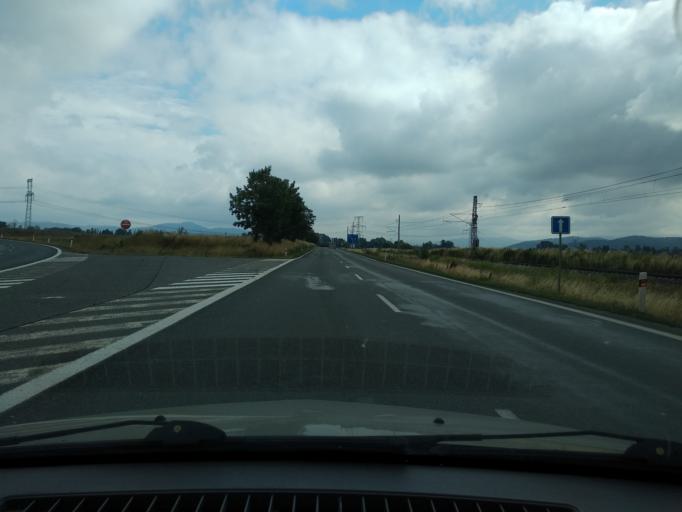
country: CZ
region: Olomoucky
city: Zabreh
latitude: 49.8907
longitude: 16.8948
